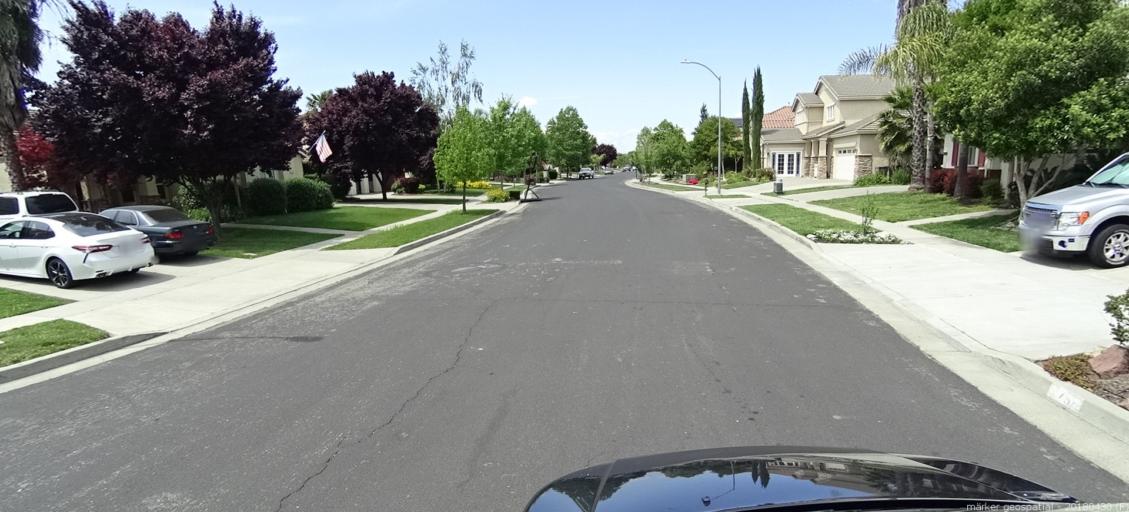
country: US
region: California
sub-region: Yolo County
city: West Sacramento
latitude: 38.5425
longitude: -121.5295
